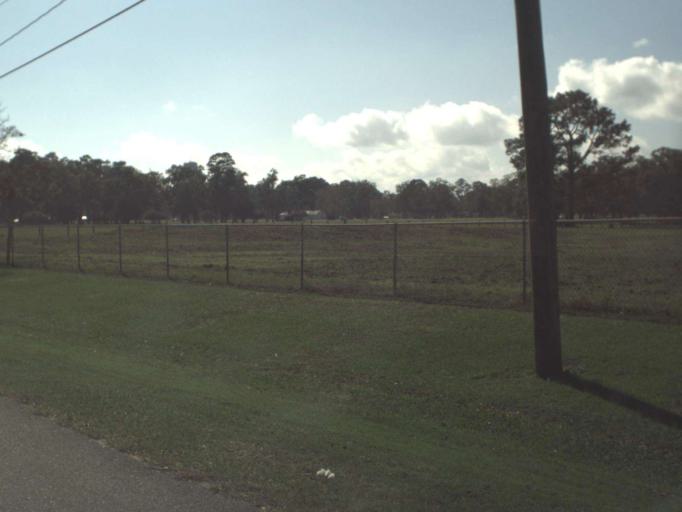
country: US
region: Florida
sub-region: Jackson County
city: Marianna
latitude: 30.8349
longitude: -85.1668
